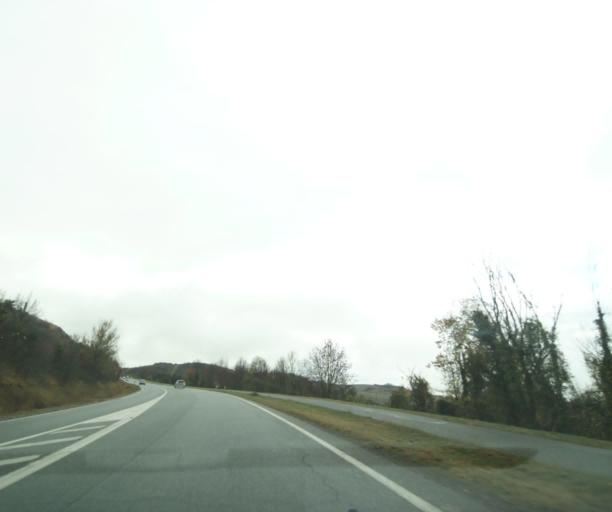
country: FR
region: Auvergne
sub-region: Departement du Puy-de-Dome
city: Cournon-d'Auvergne
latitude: 45.7523
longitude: 3.2125
